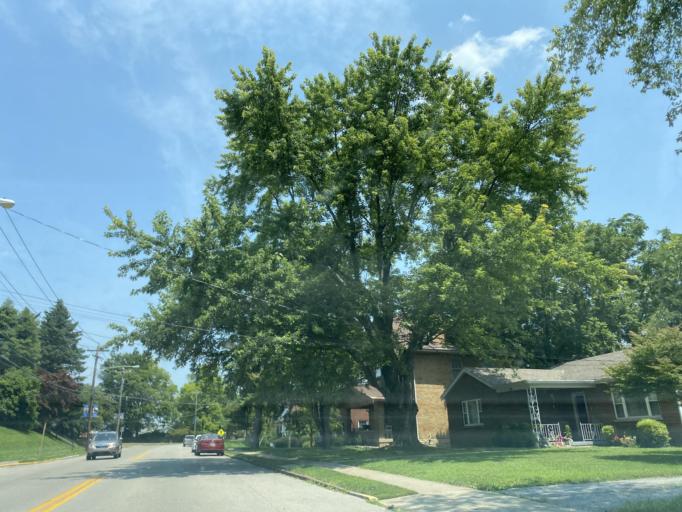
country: US
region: Kentucky
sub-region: Campbell County
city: Fort Thomas
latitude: 39.0610
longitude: -84.4502
